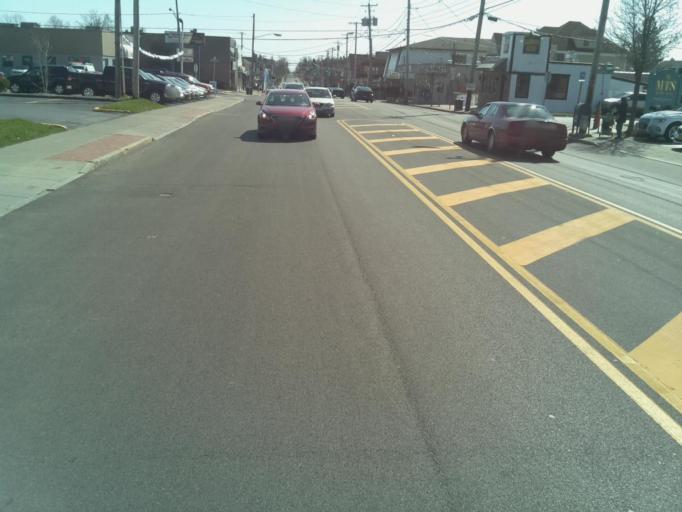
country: US
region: New York
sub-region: Onondaga County
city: Lyncourt
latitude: 43.0686
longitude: -76.1092
